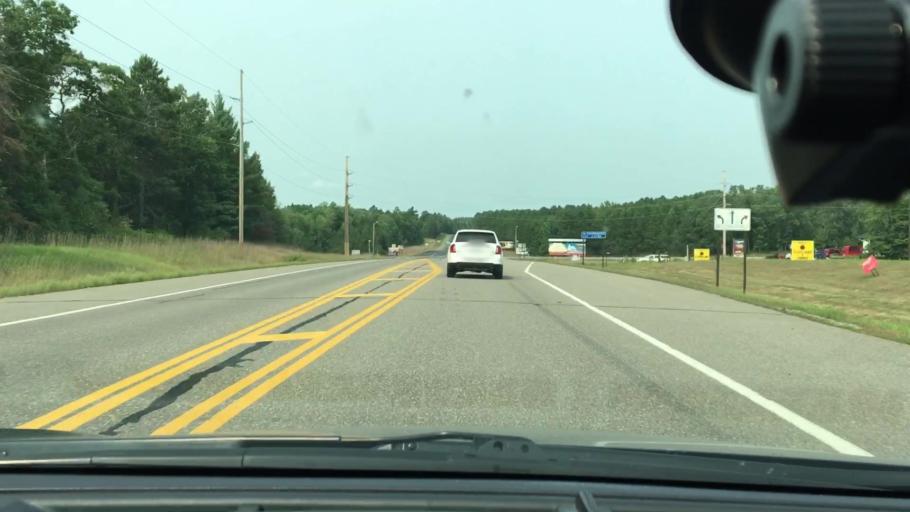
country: US
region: Minnesota
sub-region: Crow Wing County
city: Cross Lake
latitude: 46.6154
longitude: -94.1318
